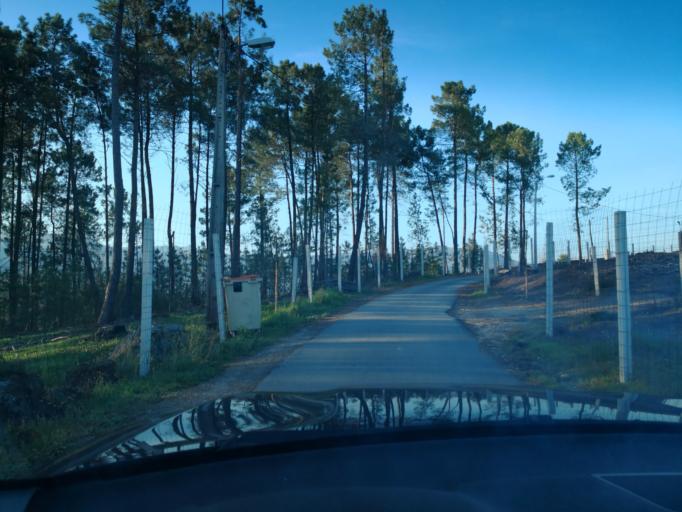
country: PT
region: Vila Real
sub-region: Vila Real
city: Vila Real
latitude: 41.2890
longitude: -7.7881
